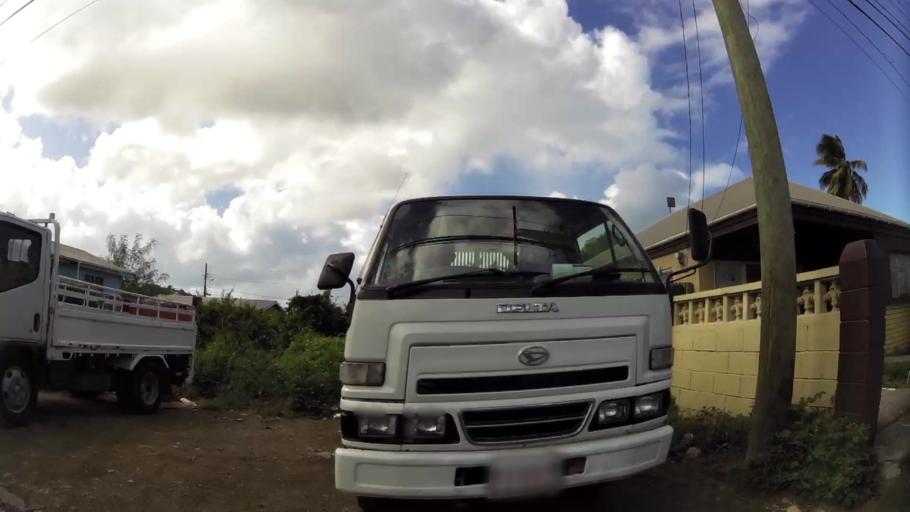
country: AG
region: Saint John
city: Saint John's
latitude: 17.1138
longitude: -61.8445
